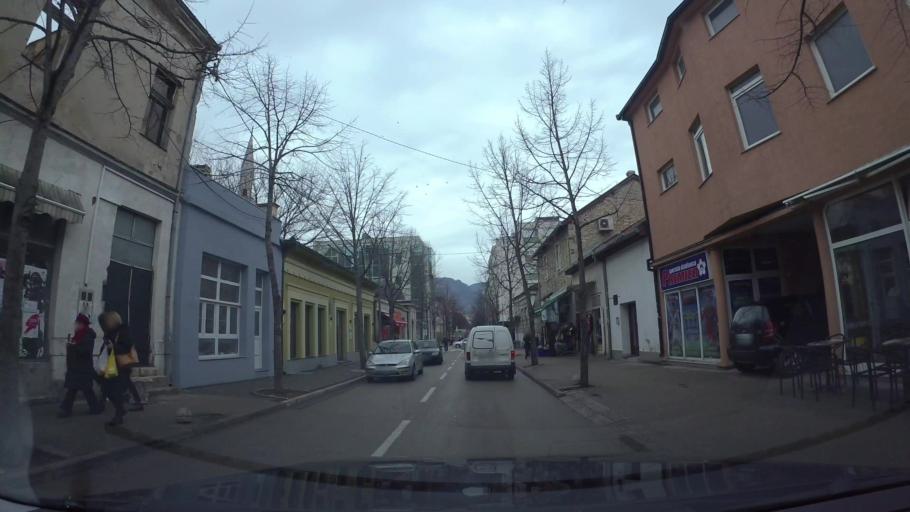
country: BA
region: Federation of Bosnia and Herzegovina
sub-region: Hercegovacko-Bosanski Kanton
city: Mostar
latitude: 43.3433
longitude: 17.8093
